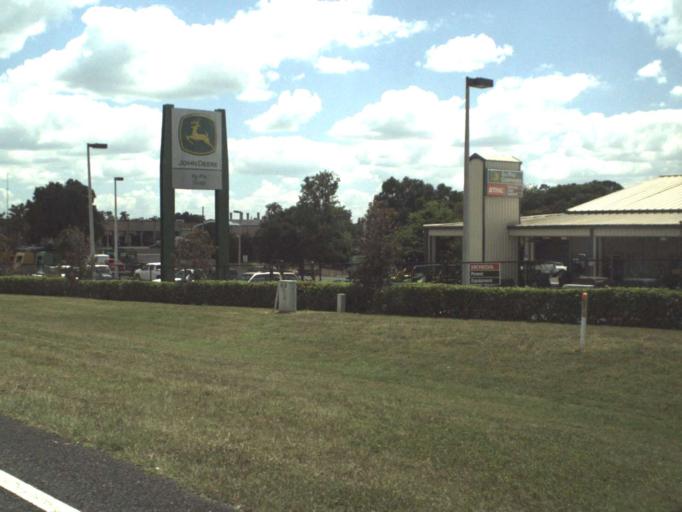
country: US
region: Florida
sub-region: Marion County
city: Ocala
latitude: 29.2542
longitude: -82.1522
